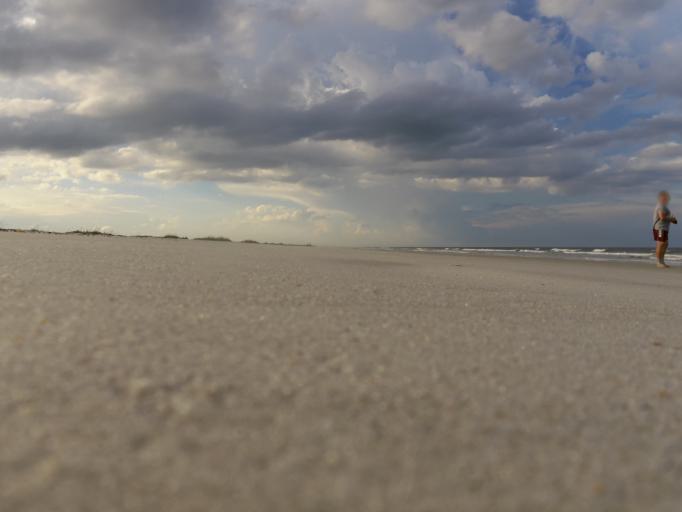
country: US
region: Florida
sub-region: Duval County
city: Atlantic Beach
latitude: 30.4498
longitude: -81.4098
